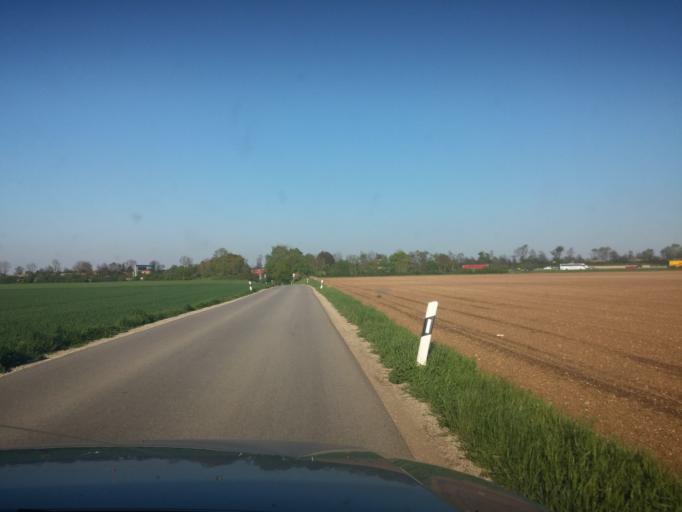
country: DE
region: Bavaria
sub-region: Upper Bavaria
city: Feldkirchen
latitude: 48.1327
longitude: 11.7546
